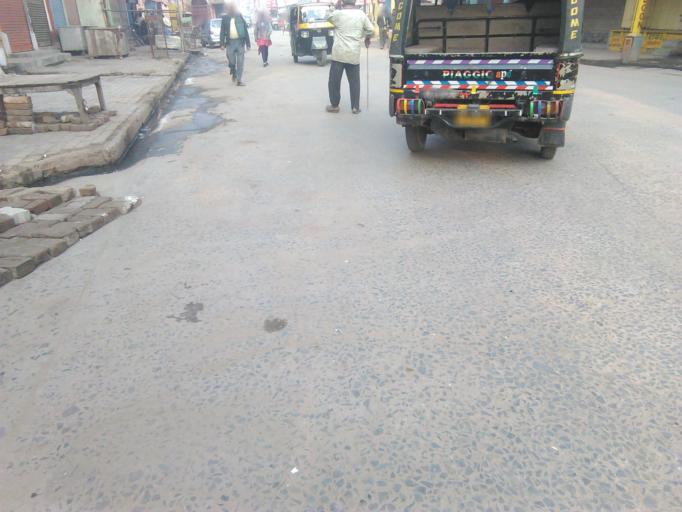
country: IN
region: Bihar
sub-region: Gaya
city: Gaya
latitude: 24.7962
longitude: 85.0101
